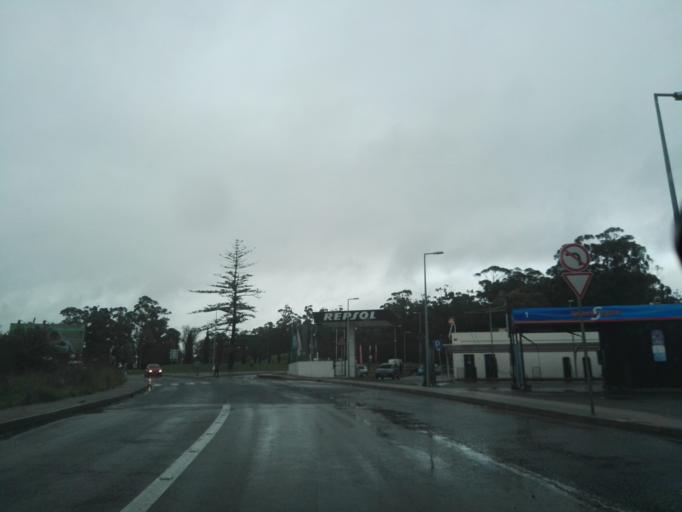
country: PT
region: Lisbon
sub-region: Odivelas
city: Pontinha
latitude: 38.7390
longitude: -9.2036
